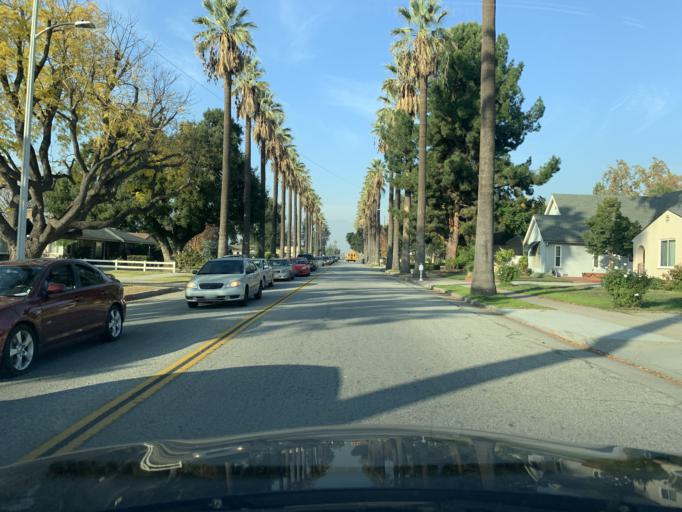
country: US
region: California
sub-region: Los Angeles County
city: Covina
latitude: 34.0873
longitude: -117.8990
